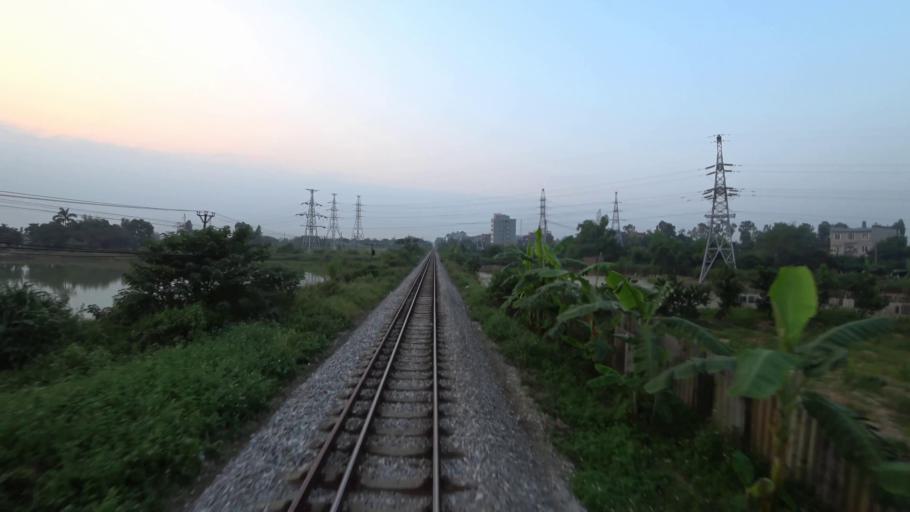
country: VN
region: Ha Noi
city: Dong Anh
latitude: 21.1470
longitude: 105.8593
